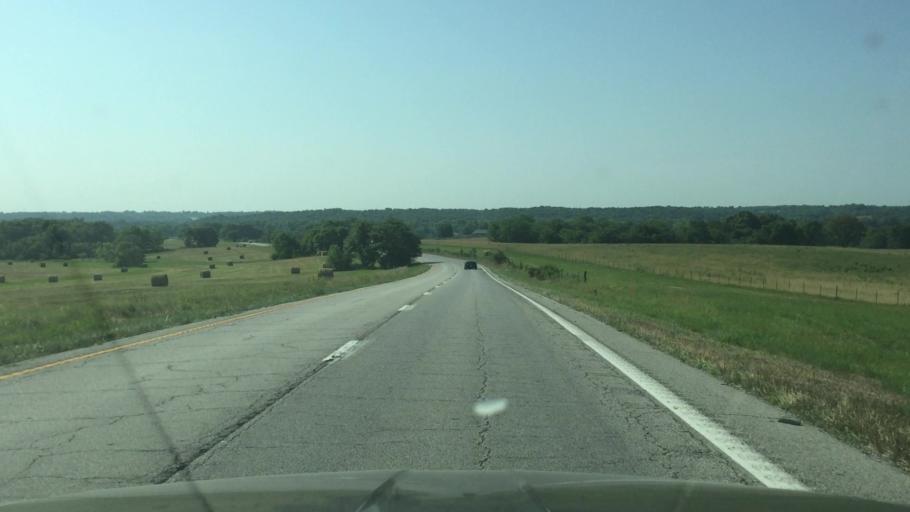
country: US
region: Missouri
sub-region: Johnson County
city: Holden
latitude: 38.8106
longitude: -93.8972
